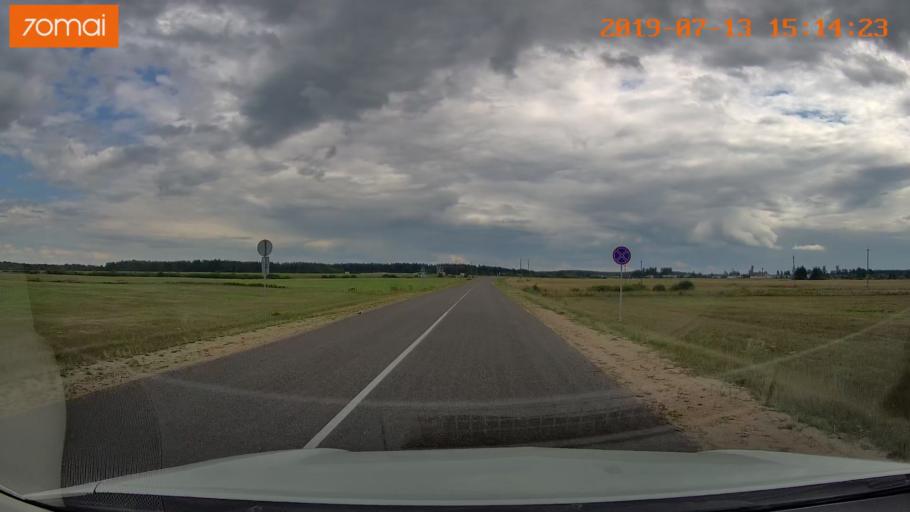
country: BY
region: Mogilev
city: Hlusha
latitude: 53.1279
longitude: 28.8184
